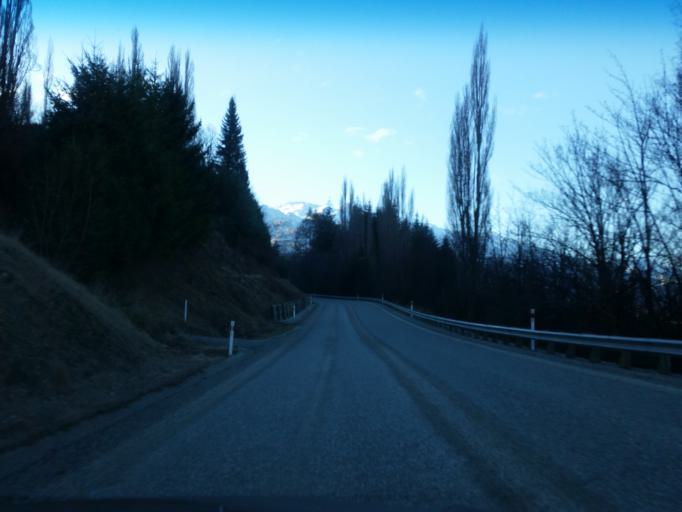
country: NZ
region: Otago
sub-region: Queenstown-Lakes District
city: Queenstown
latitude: -44.9733
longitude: 168.6964
